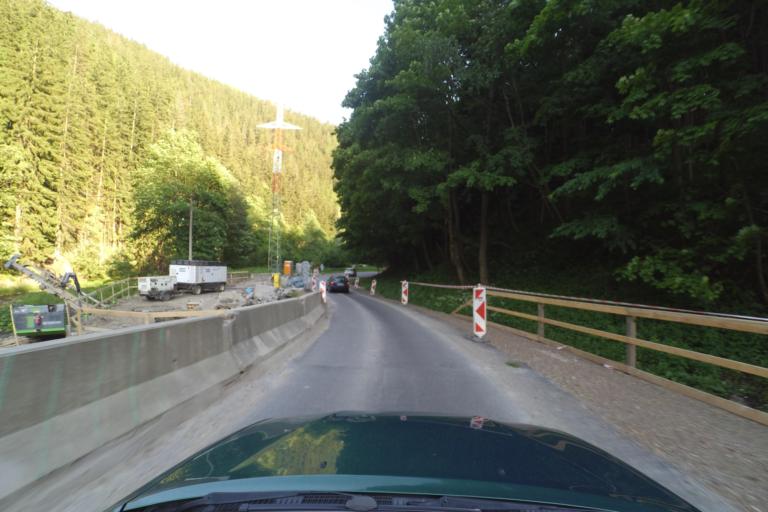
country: CZ
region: Kralovehradecky
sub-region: Okres Trutnov
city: Svoboda nad Upou
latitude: 50.6720
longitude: 15.7942
